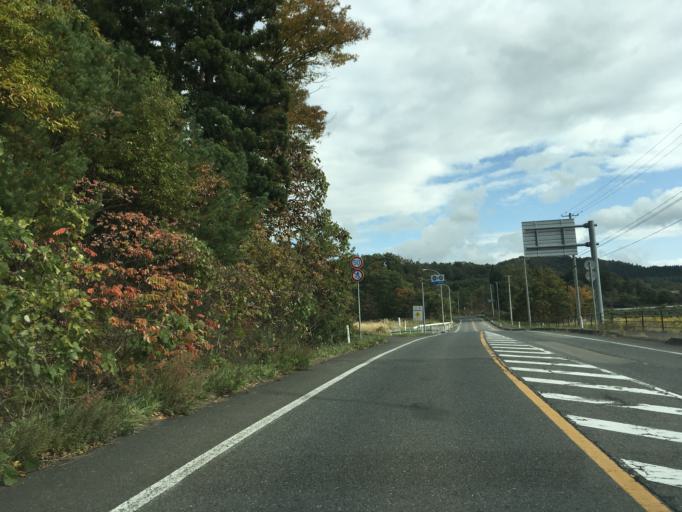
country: JP
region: Iwate
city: Hanamaki
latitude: 39.3939
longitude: 141.1664
